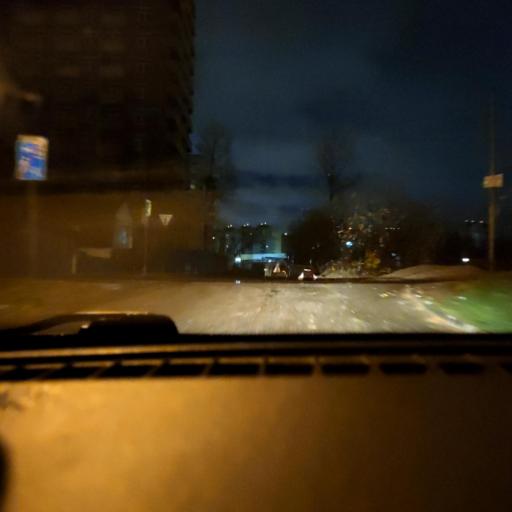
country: RU
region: Perm
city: Perm
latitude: 57.9733
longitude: 56.1932
